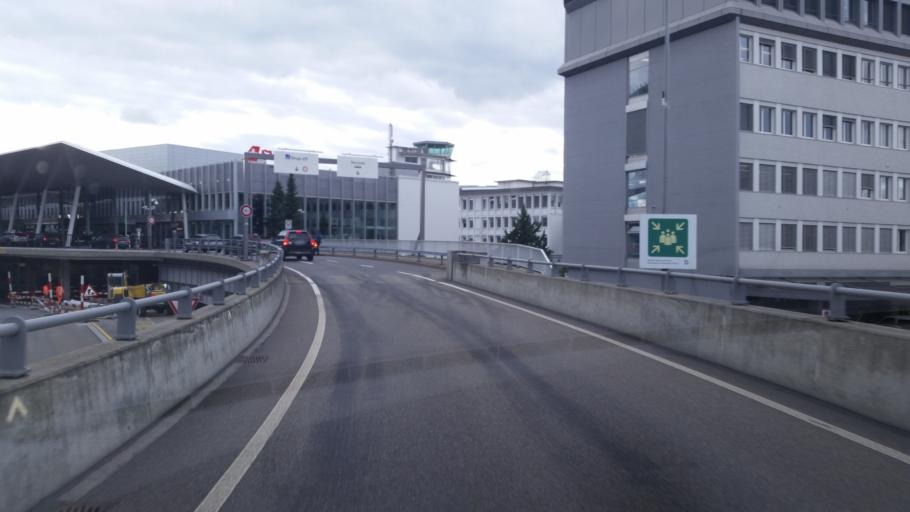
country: CH
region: Zurich
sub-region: Bezirk Buelach
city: Kloten / Holberg
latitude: 47.4532
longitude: 8.5641
